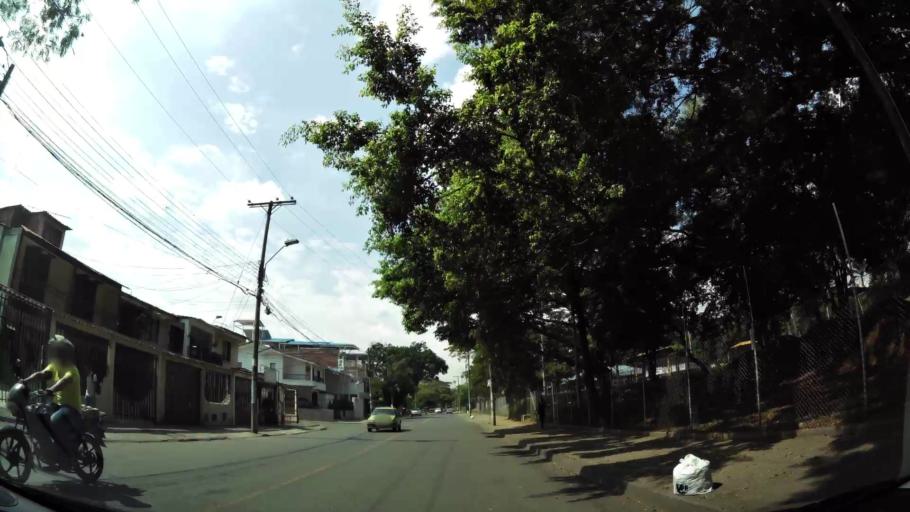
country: CO
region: Valle del Cauca
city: Cali
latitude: 3.4902
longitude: -76.5011
